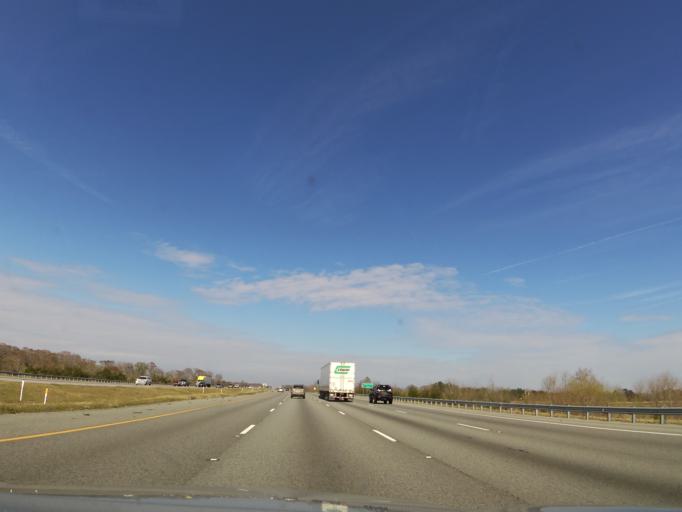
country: US
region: Georgia
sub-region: McIntosh County
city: Darien
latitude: 31.3458
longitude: -81.4625
